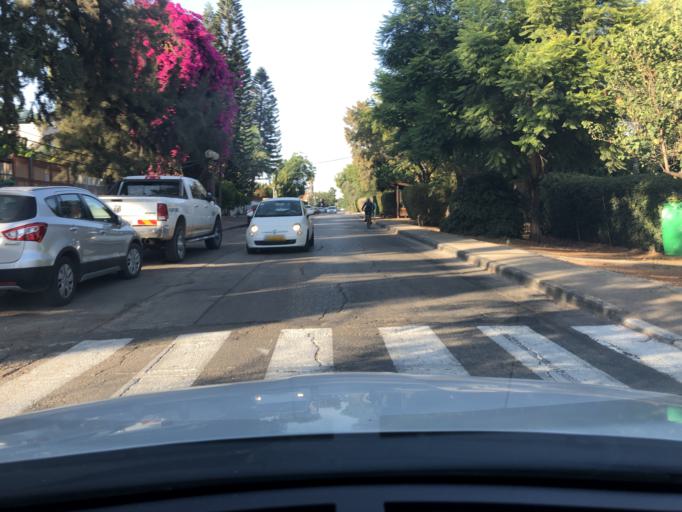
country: IL
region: Central District
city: Hod HaSharon
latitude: 32.1362
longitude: 34.9026
